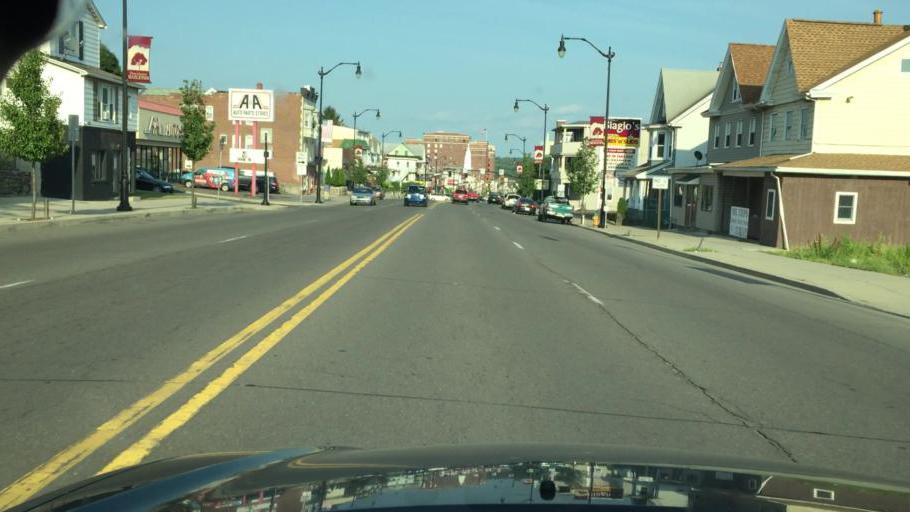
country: US
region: Pennsylvania
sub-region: Luzerne County
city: Hazleton
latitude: 40.9563
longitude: -75.9827
